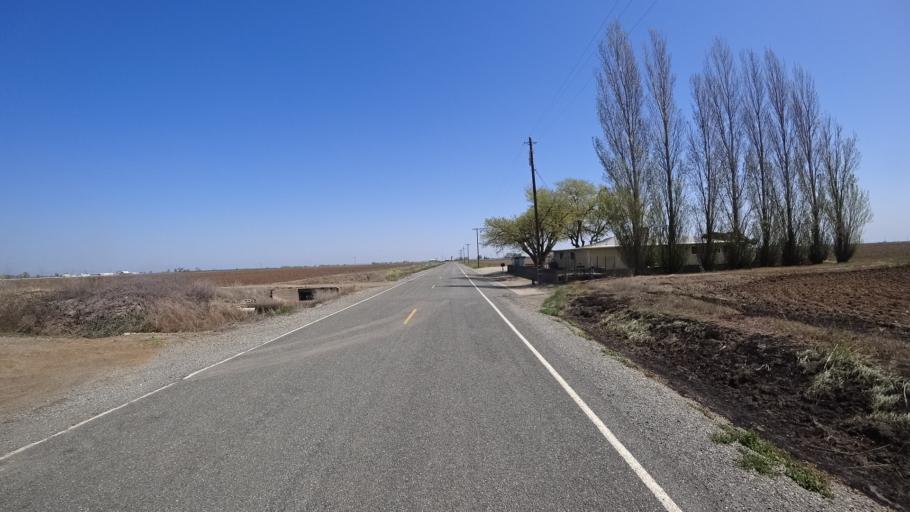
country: US
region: California
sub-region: Glenn County
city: Willows
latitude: 39.4947
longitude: -122.1420
